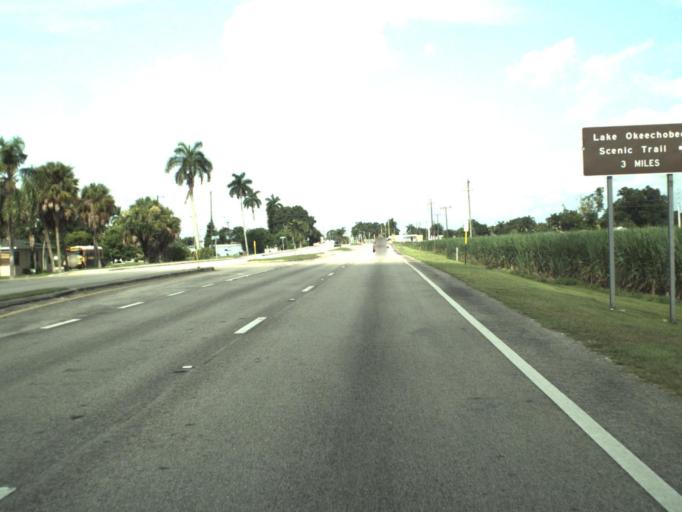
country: US
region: Florida
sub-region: Palm Beach County
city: South Bay
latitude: 26.6643
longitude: -80.7085
